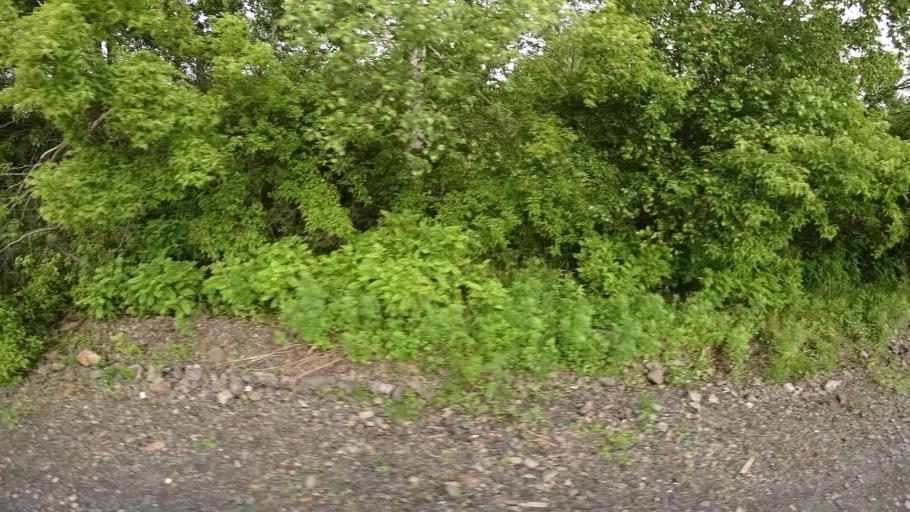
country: RU
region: Khabarovsk Krai
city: Amursk
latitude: 49.8903
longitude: 136.1298
